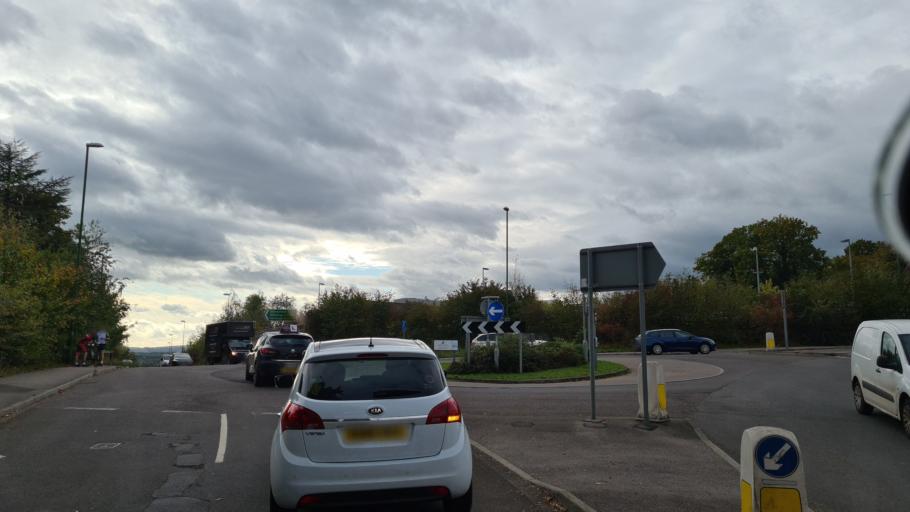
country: GB
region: England
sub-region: West Sussex
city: Haywards Heath
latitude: 50.9919
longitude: -0.0871
